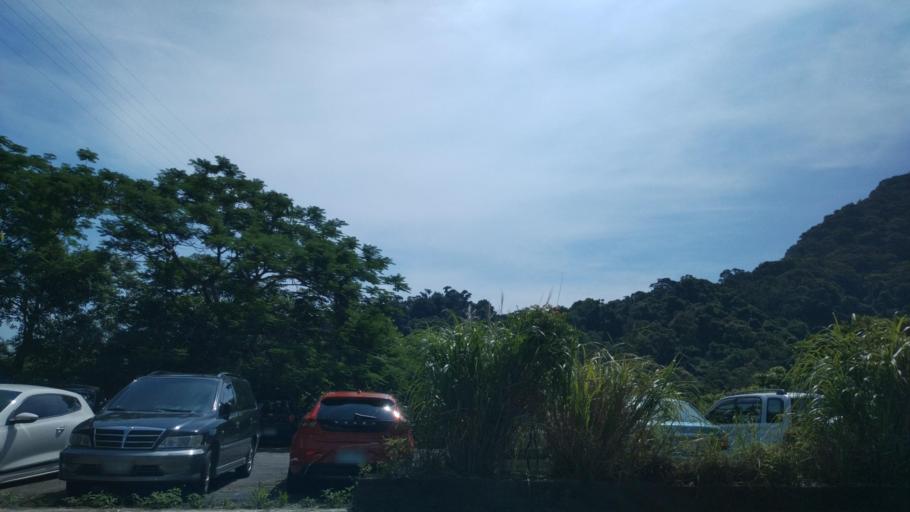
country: TW
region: Taipei
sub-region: Taipei
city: Banqiao
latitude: 24.9415
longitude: 121.5046
